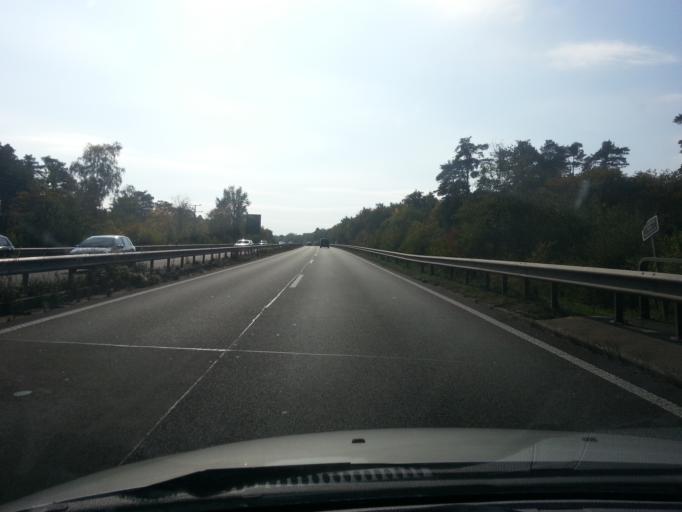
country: DE
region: Rheinland-Pfalz
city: Speyer
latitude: 49.3425
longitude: 8.4130
